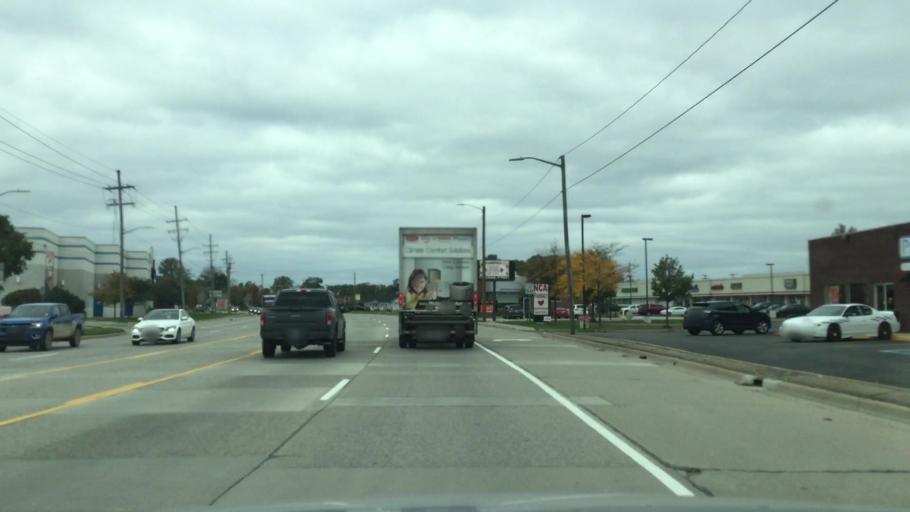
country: US
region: Michigan
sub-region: Oakland County
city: Waterford
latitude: 42.6609
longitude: -83.4325
